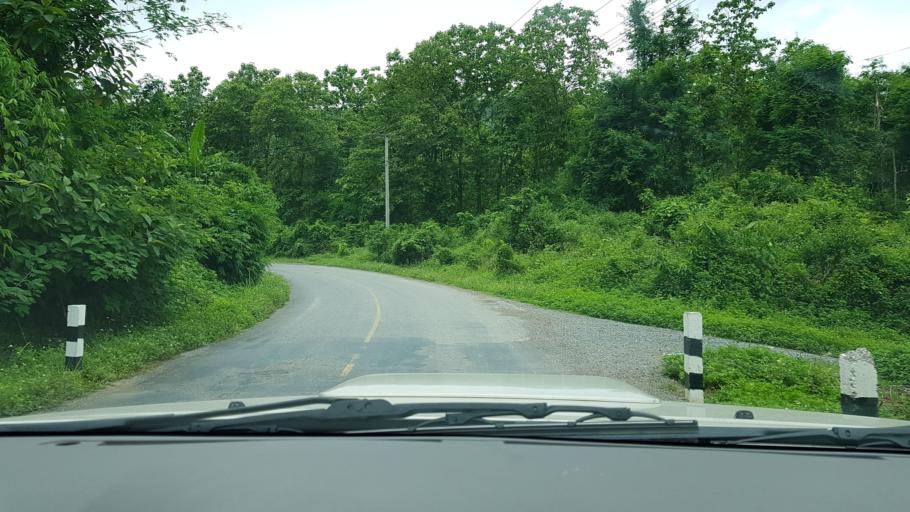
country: LA
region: Loungnamtha
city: Muang Nale
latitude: 20.1949
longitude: 101.5240
